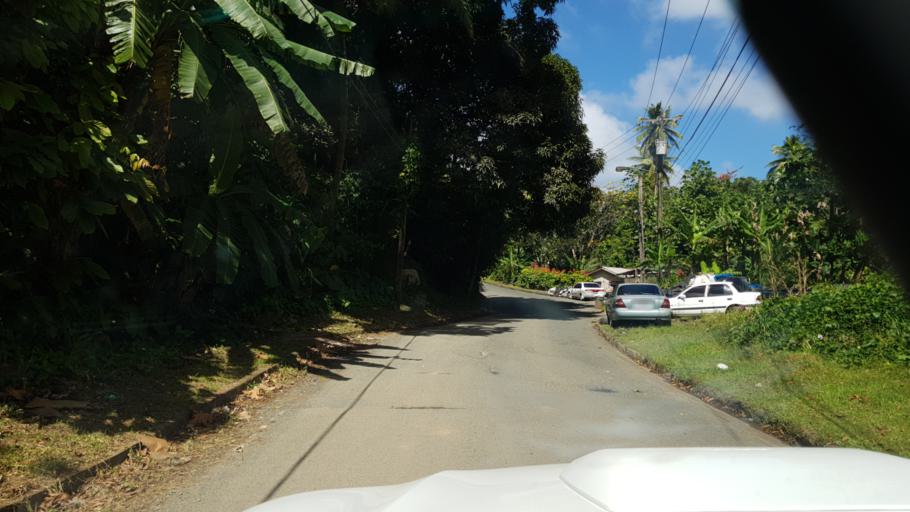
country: LC
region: Castries Quarter
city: Castries
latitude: 13.9798
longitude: -60.9743
